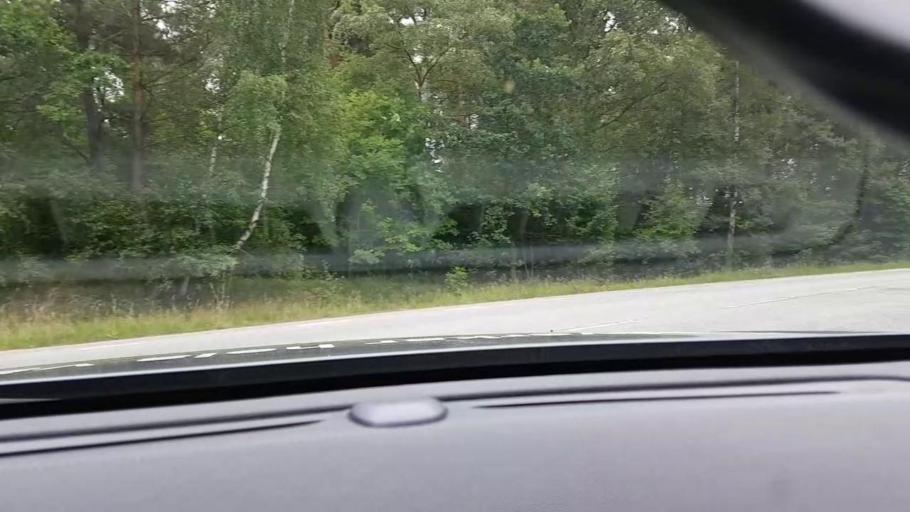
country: SE
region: Skane
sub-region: Hassleholms Kommun
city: Hassleholm
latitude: 56.1717
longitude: 13.8024
